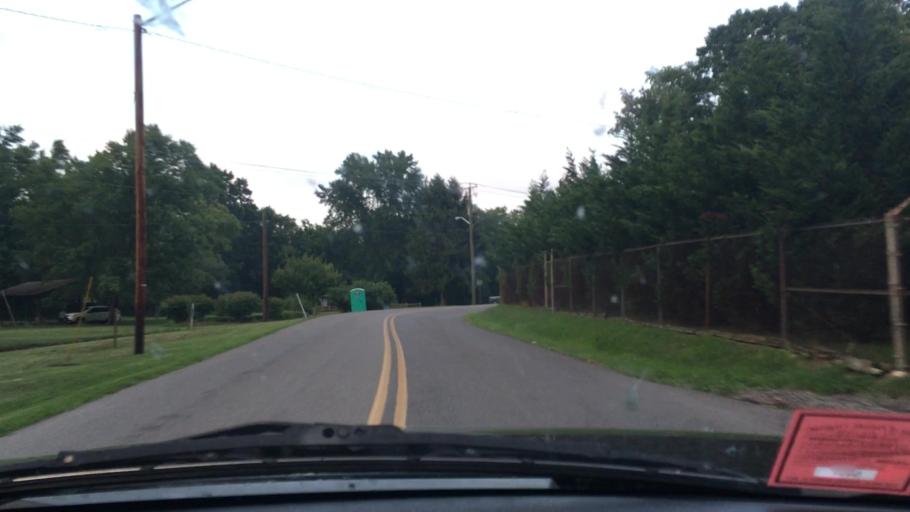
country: US
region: Virginia
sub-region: Pulaski County
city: Pulaski
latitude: 37.0435
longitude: -80.7627
